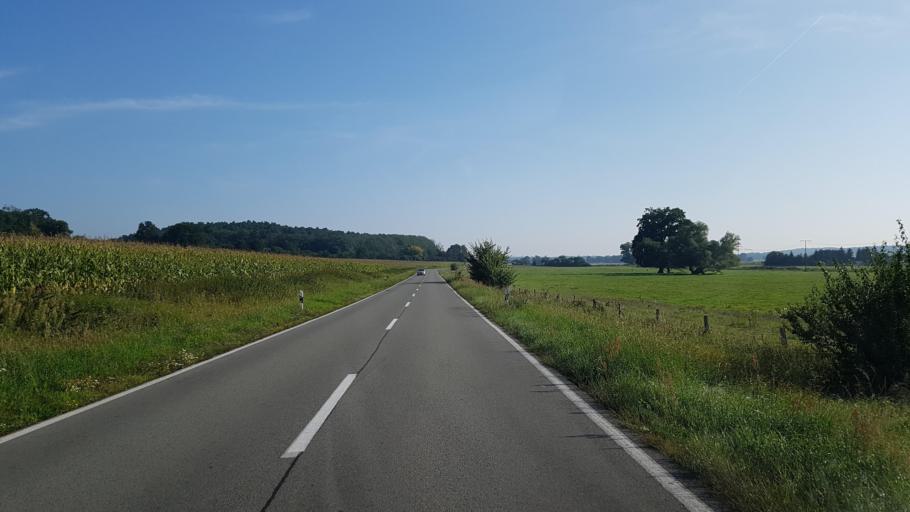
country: DE
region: Brandenburg
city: Pawesin
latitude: 52.4990
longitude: 12.6209
